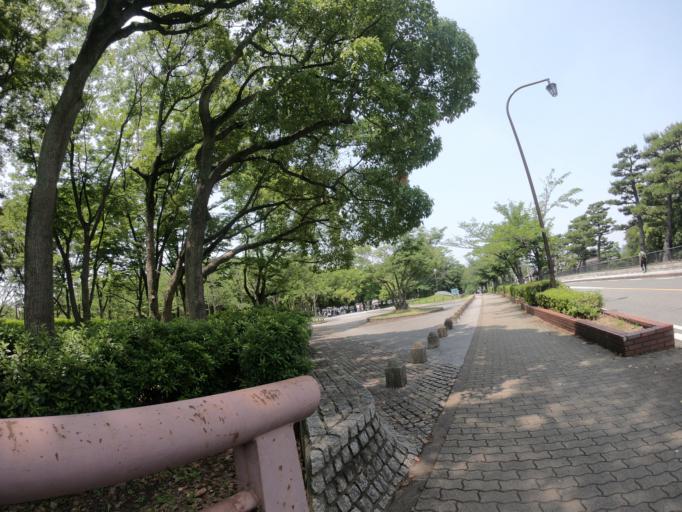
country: JP
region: Osaka
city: Sakai
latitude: 34.5617
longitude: 135.4829
